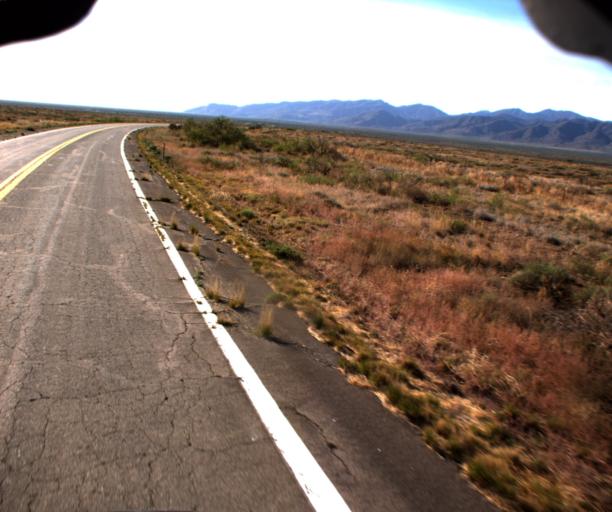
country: US
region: Arizona
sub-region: Cochise County
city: Willcox
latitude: 32.3710
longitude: -109.6272
